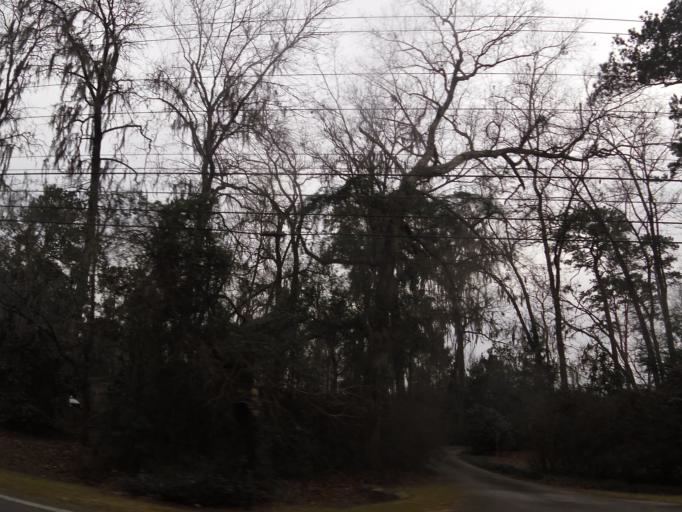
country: US
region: Georgia
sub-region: Thomas County
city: Thomasville
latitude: 30.8112
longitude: -83.9571
